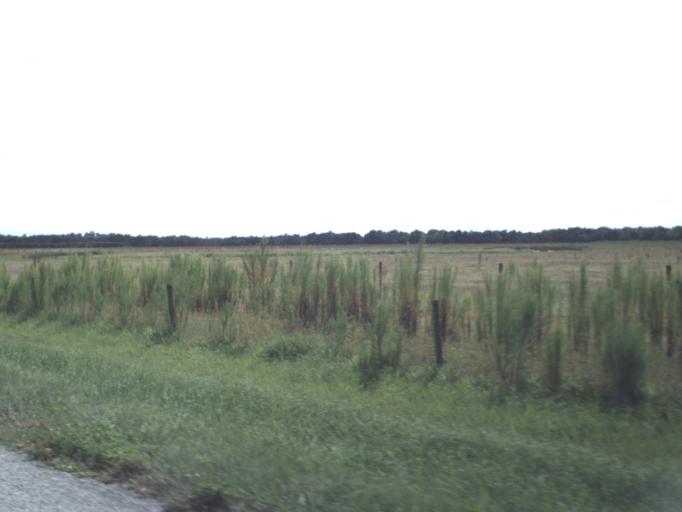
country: US
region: Florida
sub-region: Hardee County
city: Zolfo Springs
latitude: 27.3961
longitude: -81.7949
